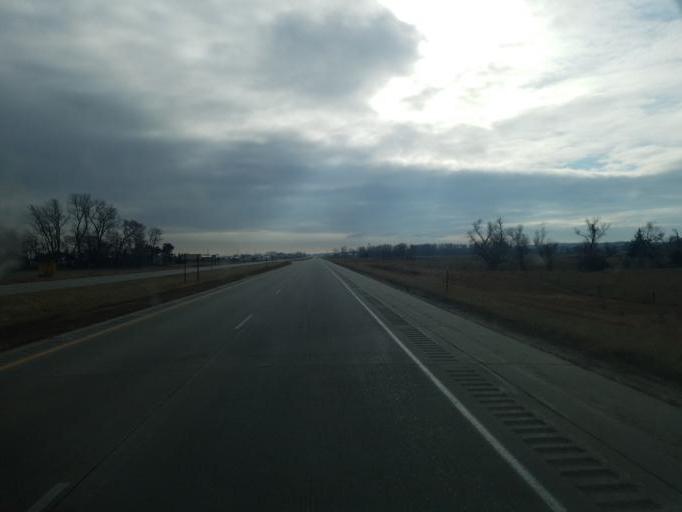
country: US
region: Nebraska
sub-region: Madison County
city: Norfolk
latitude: 42.1039
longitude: -97.4267
